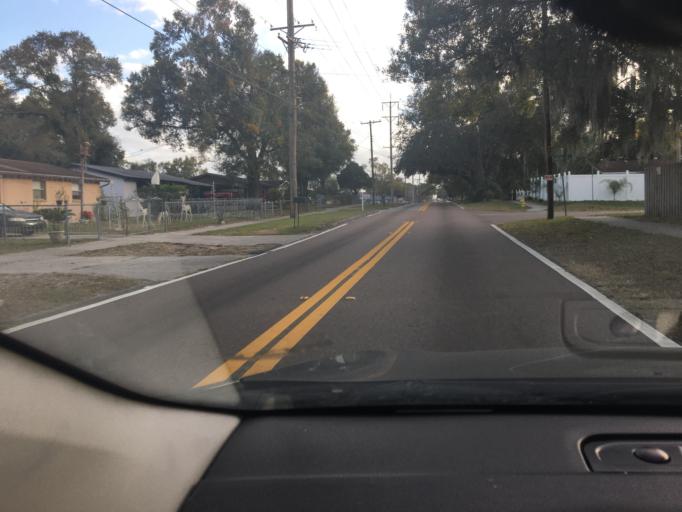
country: US
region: Florida
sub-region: Hillsborough County
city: University
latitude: 28.0352
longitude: -82.4347
